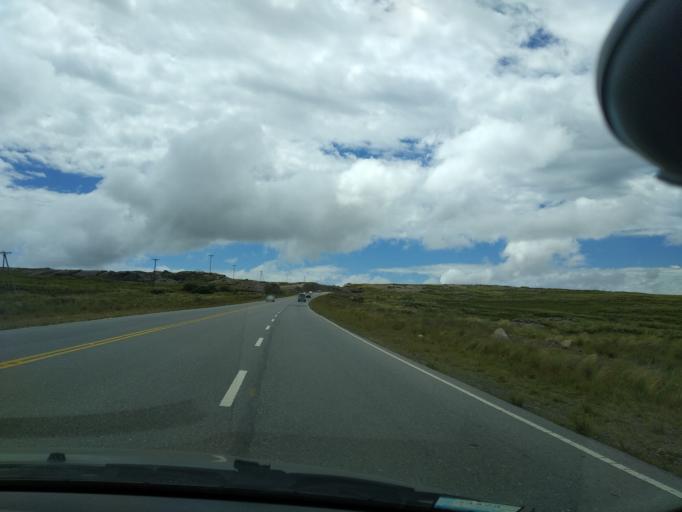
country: AR
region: Cordoba
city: Mina Clavero
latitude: -31.6101
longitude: -64.8342
